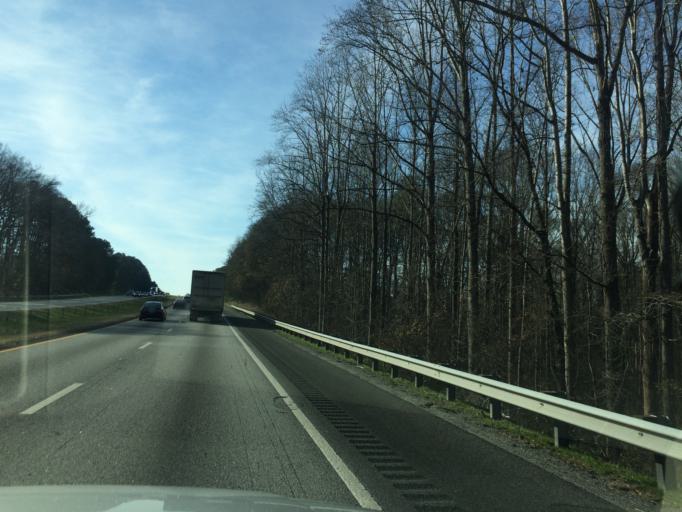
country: US
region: Georgia
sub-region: Hart County
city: Reed Creek
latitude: 34.5105
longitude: -82.9469
